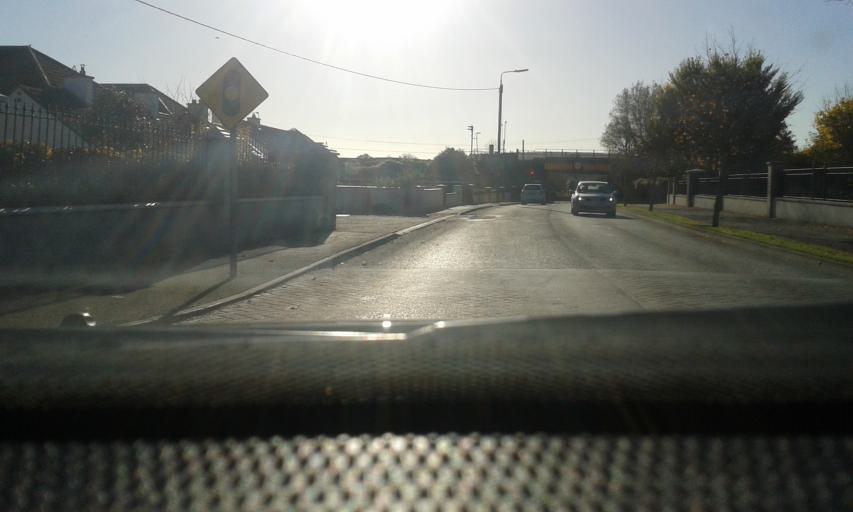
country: IE
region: Leinster
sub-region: Kildare
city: Monasterevin
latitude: 53.1477
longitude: -7.0558
